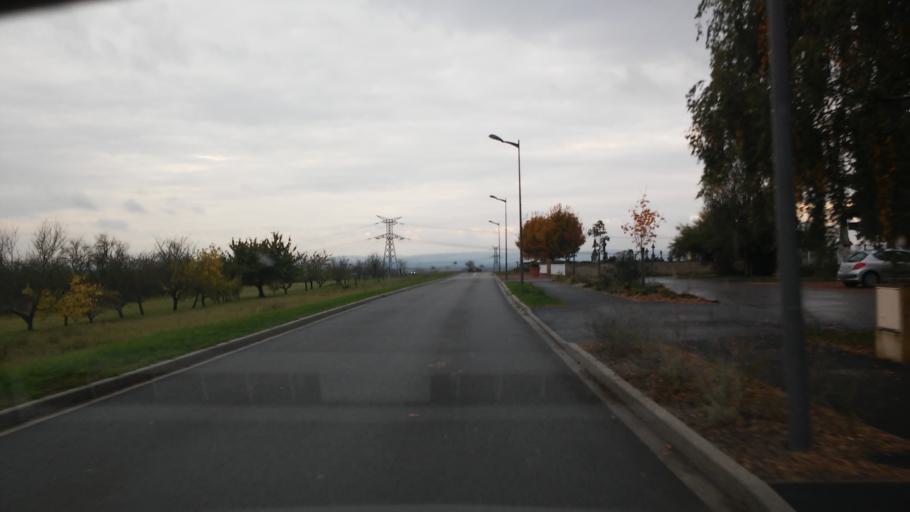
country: FR
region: Lorraine
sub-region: Departement de la Moselle
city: Vigy
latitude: 49.2046
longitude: 6.2901
